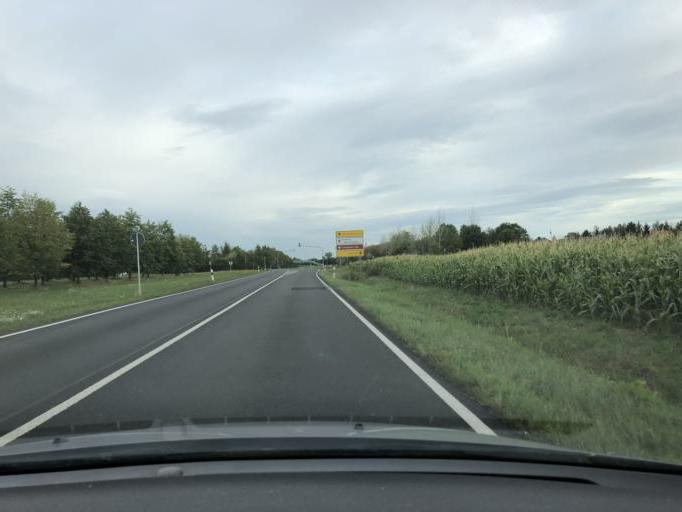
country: DE
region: Saxony
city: Rackwitz
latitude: 51.4305
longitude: 12.3705
